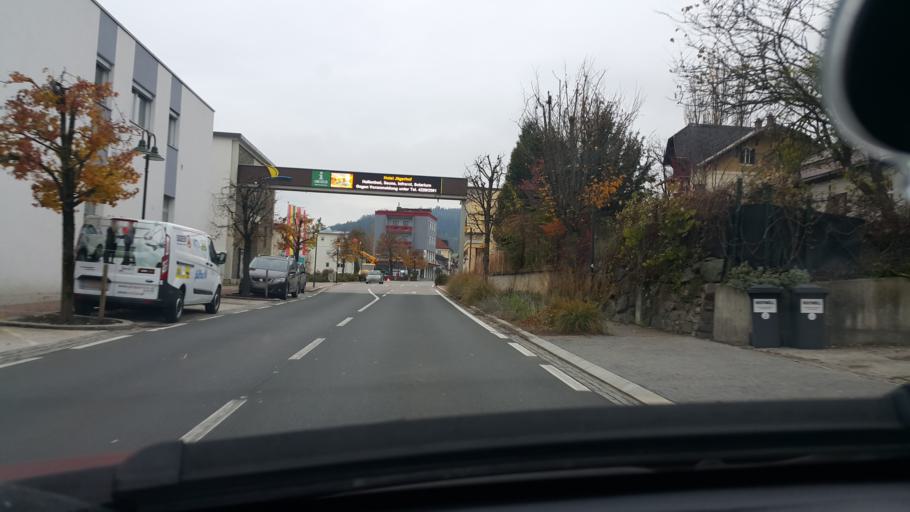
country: AT
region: Carinthia
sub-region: Politischer Bezirk Klagenfurt Land
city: Keutschach am See
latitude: 46.6263
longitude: 14.2151
